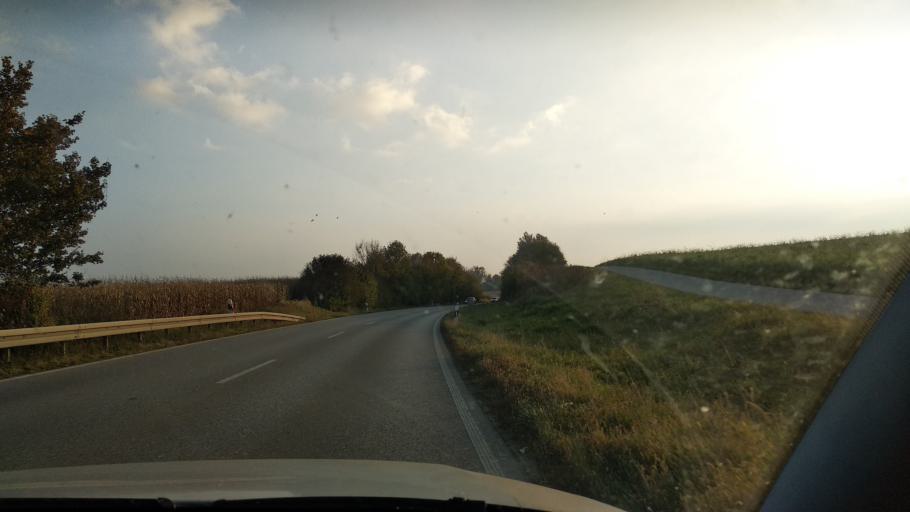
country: DE
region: Bavaria
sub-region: Upper Bavaria
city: Markt Schwaben
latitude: 48.1751
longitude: 11.8651
